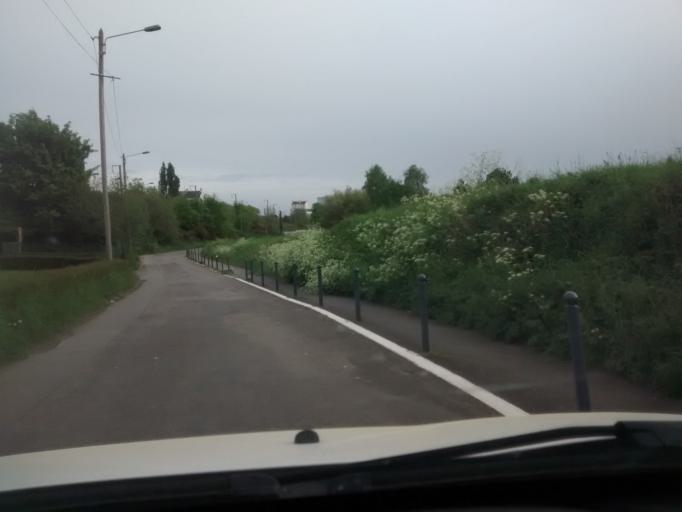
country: FR
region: Brittany
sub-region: Departement d'Ille-et-Vilaine
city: Rennes
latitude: 48.1248
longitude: -1.6890
